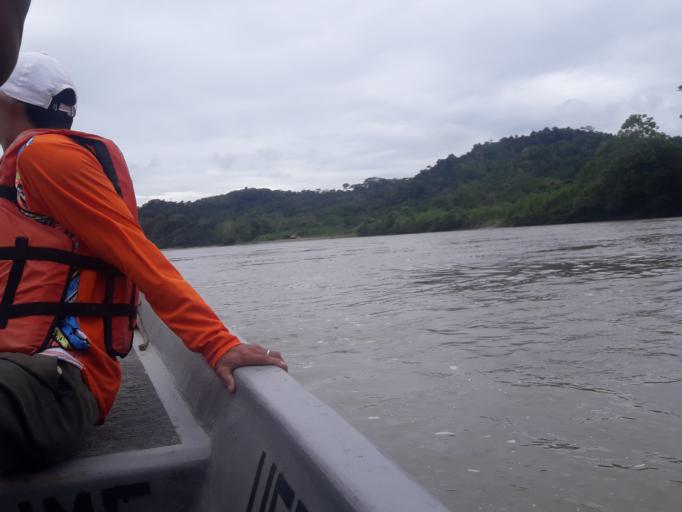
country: EC
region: Orellana
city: Boca Suno
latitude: -0.8811
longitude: -77.2821
